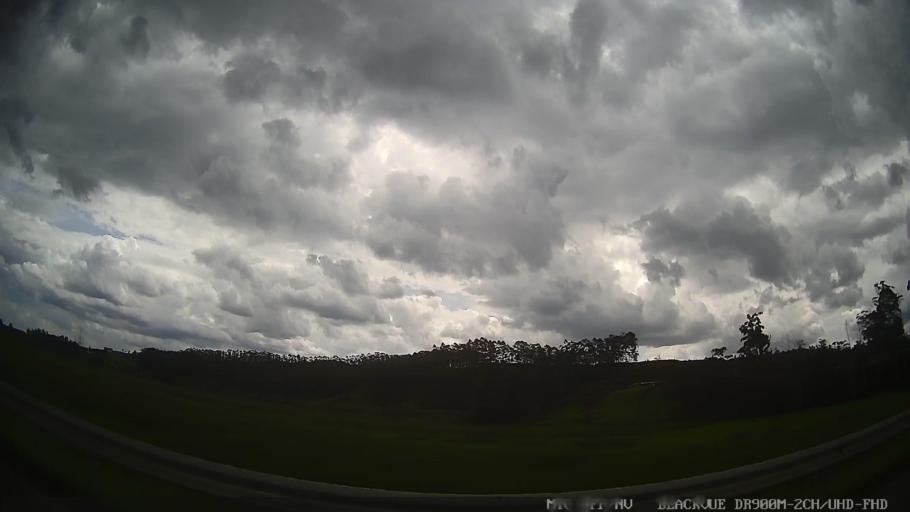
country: BR
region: Sao Paulo
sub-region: Suzano
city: Suzano
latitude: -23.6129
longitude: -46.2983
